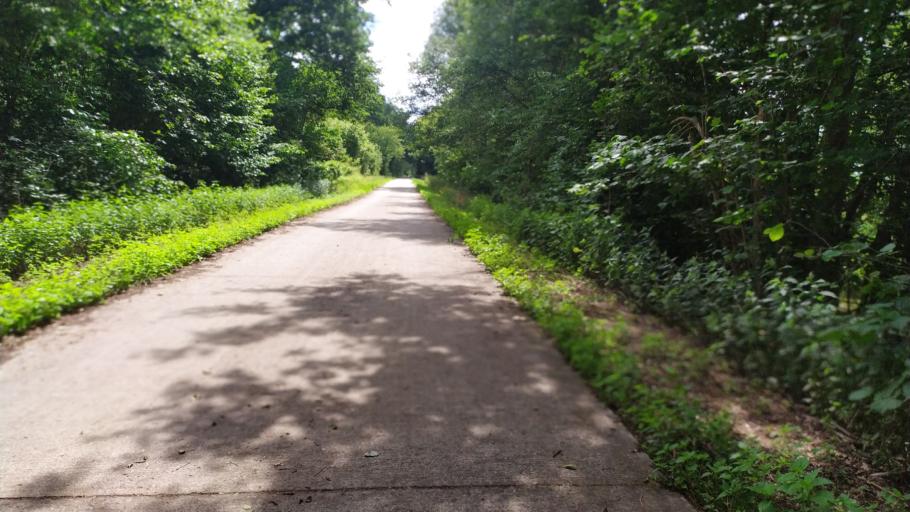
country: BE
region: Wallonia
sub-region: Province du Luxembourg
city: Wellin
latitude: 50.1566
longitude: 5.1211
